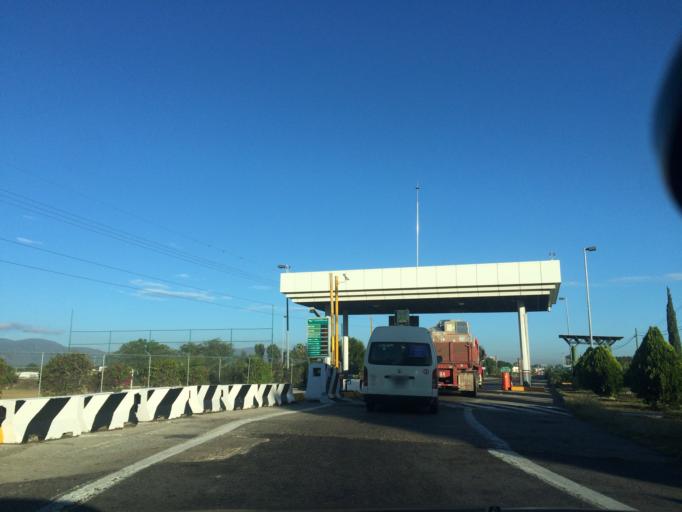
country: MX
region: Puebla
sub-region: Santiago Miahuatlan
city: San Jose Monte Chiquito
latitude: 18.4874
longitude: -97.4566
